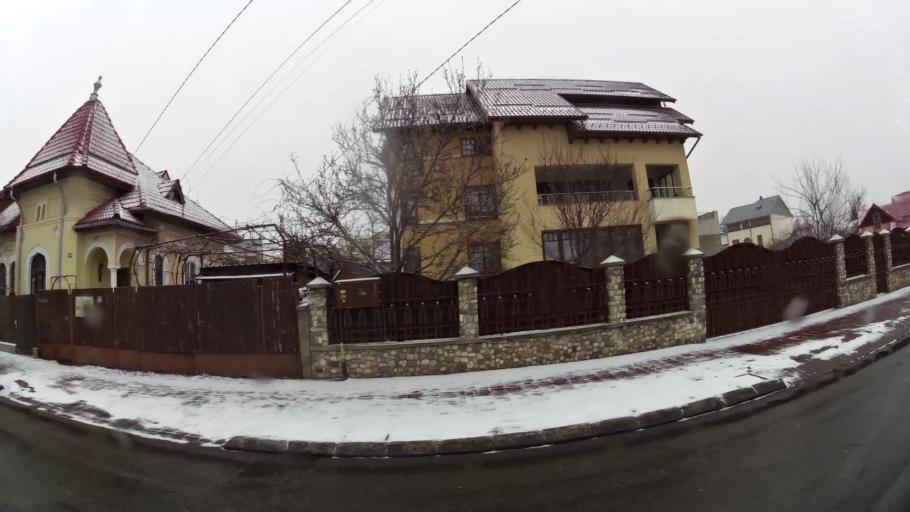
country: RO
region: Dambovita
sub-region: Municipiul Targoviste
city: Targoviste
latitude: 44.9276
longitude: 25.4505
